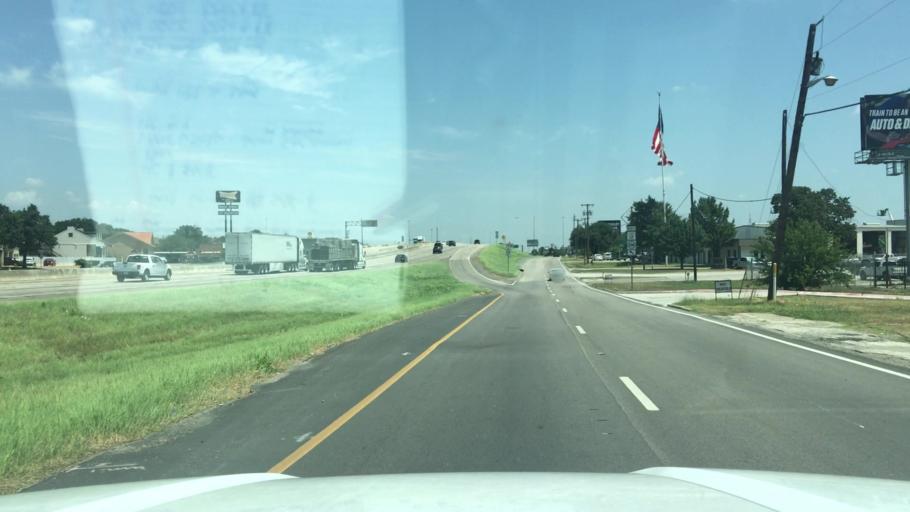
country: US
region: Texas
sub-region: Dallas County
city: Irving
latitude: 32.8266
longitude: -96.9183
